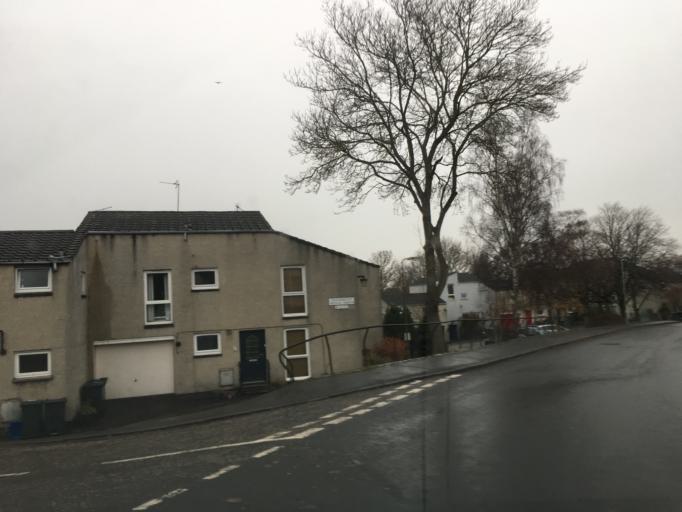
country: GB
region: Scotland
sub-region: Edinburgh
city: Currie
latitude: 55.9561
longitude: -3.3014
